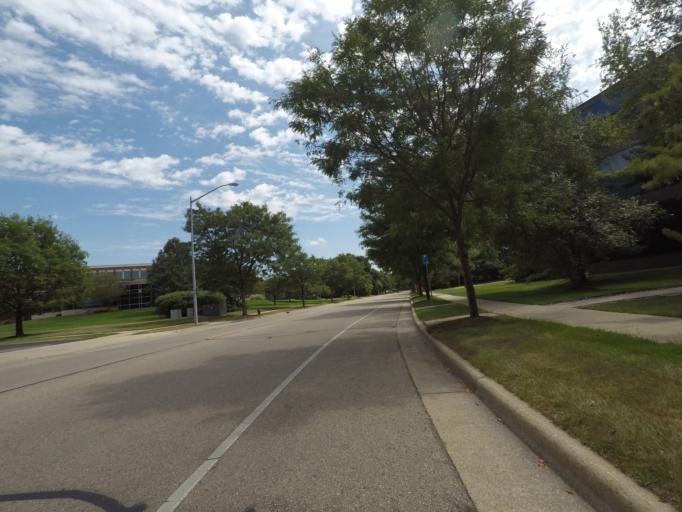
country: US
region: Wisconsin
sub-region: Dane County
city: Middleton
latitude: 43.0794
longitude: -89.5333
